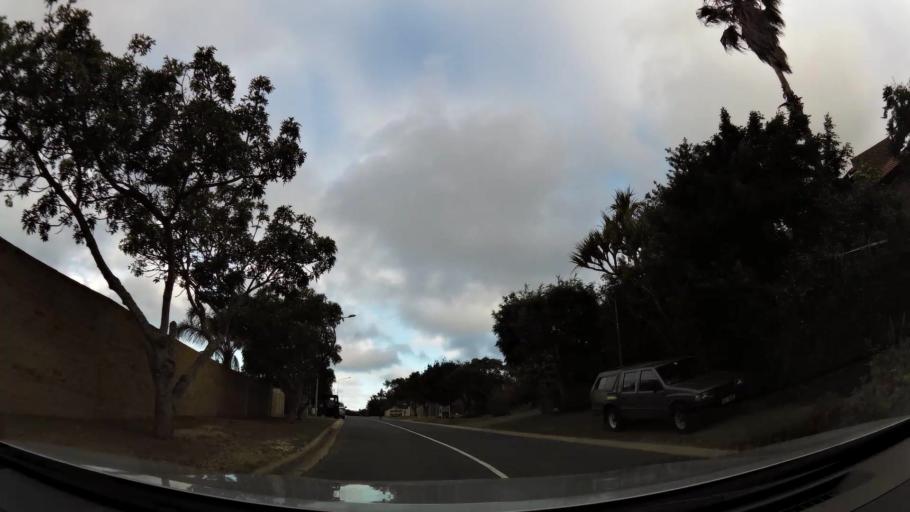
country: ZA
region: Western Cape
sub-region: Eden District Municipality
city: Plettenberg Bay
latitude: -34.0535
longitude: 23.3631
